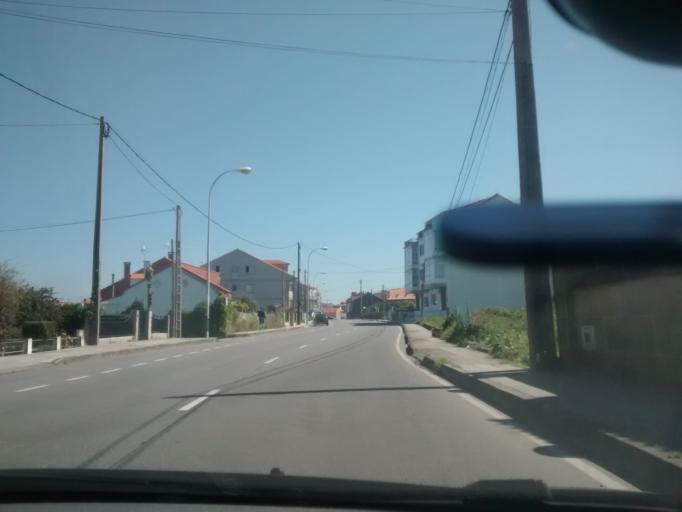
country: ES
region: Galicia
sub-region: Provincia de Pontevedra
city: O Grove
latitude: 42.4910
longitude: -8.8735
